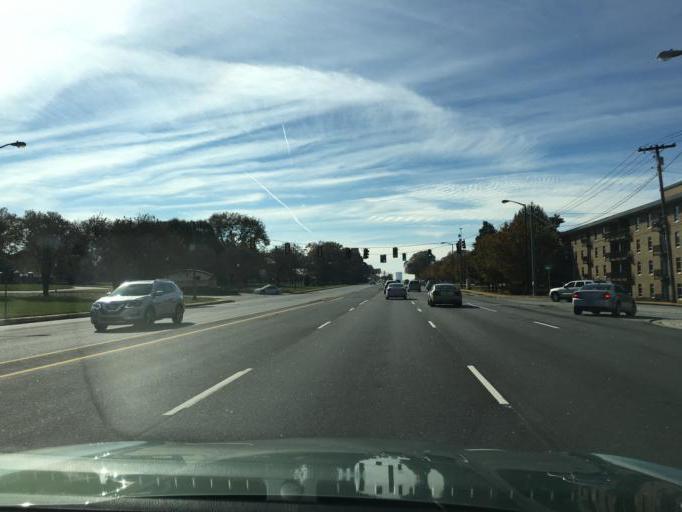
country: US
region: South Carolina
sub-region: Greenville County
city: Greenville
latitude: 34.8766
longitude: -82.3642
